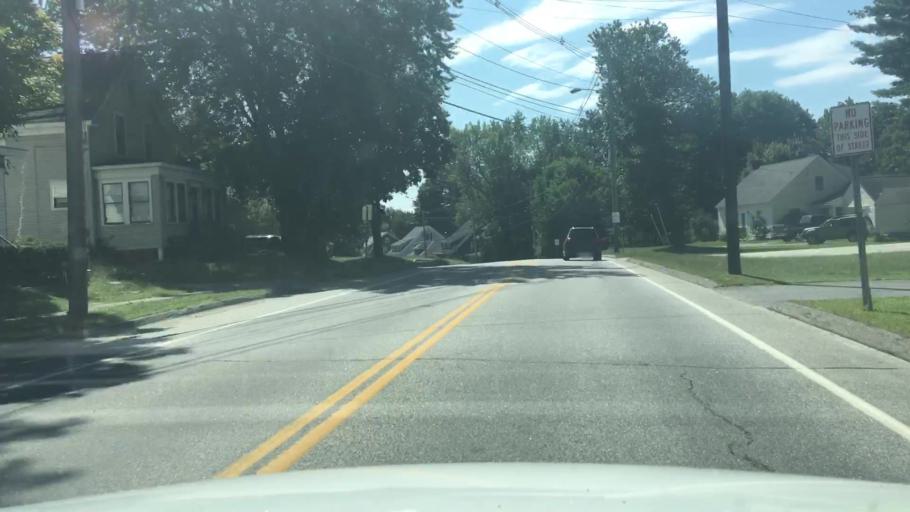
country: US
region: Maine
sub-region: Androscoggin County
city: Auburn
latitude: 44.1108
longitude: -70.2332
